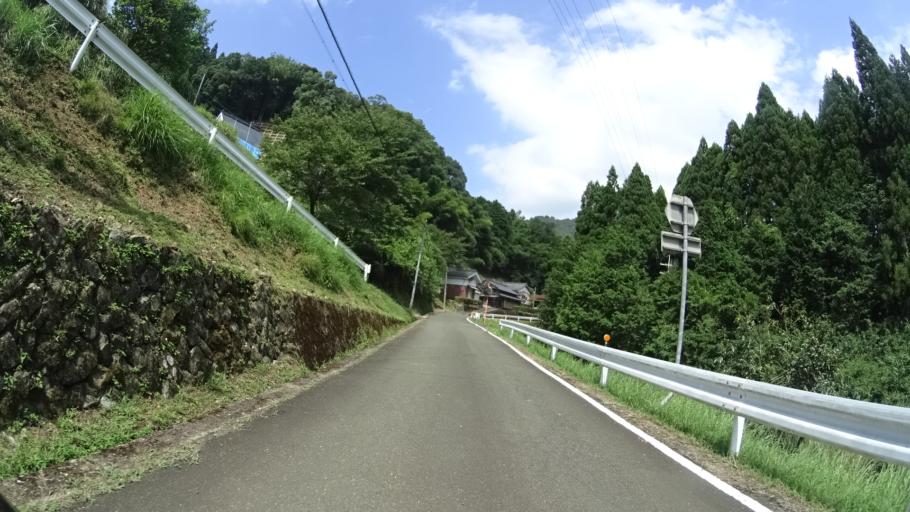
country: JP
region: Kyoto
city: Maizuru
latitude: 35.3843
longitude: 135.3571
